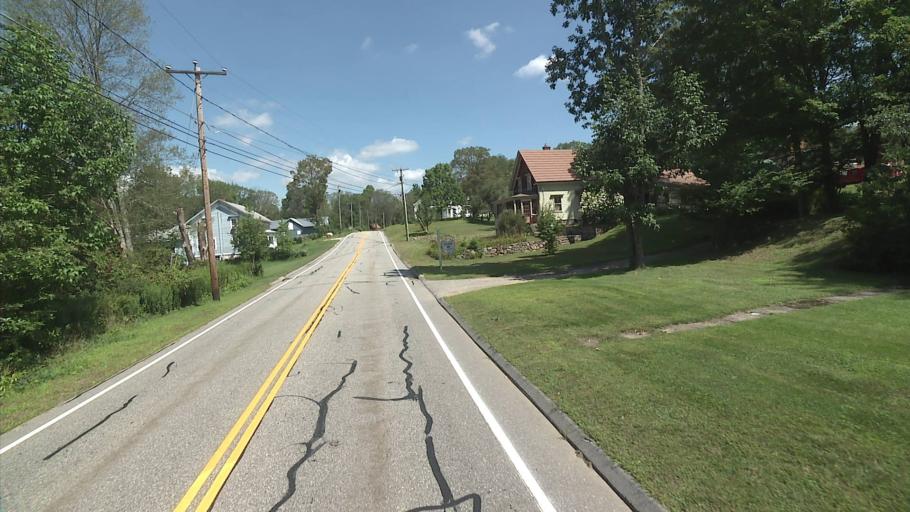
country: US
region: Connecticut
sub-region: Windham County
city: South Woodstock
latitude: 41.9049
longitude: -72.0792
